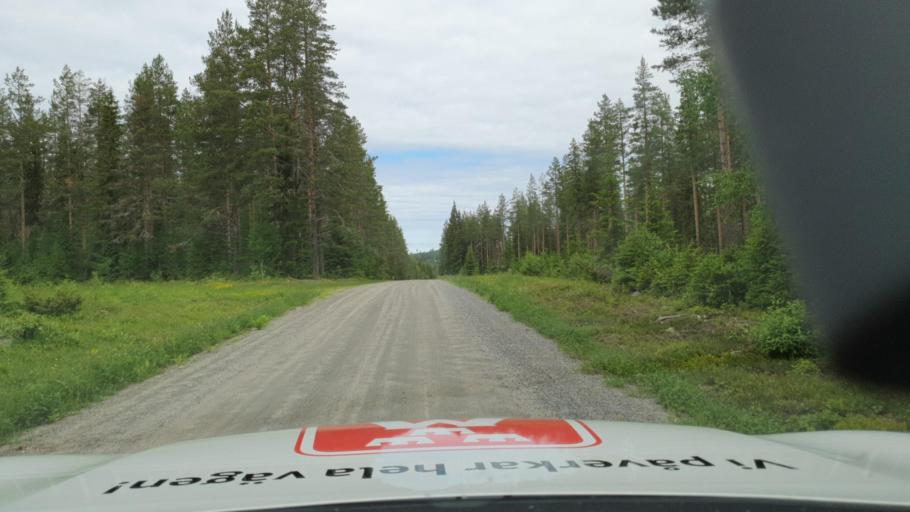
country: SE
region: Vaesterbotten
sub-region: Skelleftea Kommun
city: Langsele
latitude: 64.4638
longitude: 20.2756
